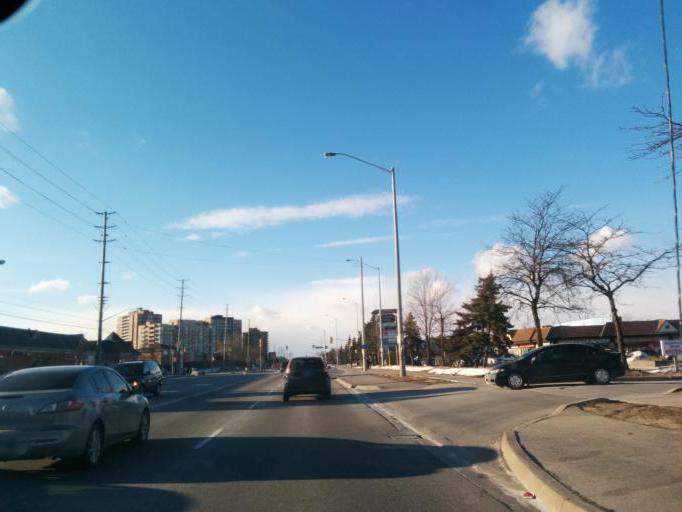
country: CA
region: Ontario
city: Brampton
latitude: 43.6502
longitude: -79.7349
